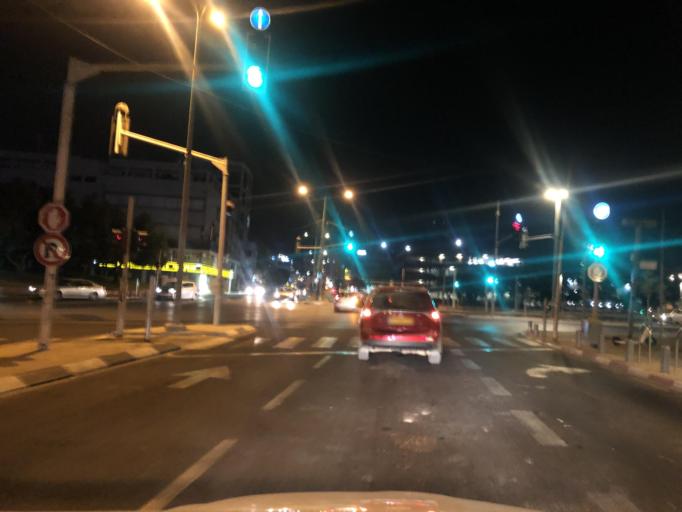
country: IL
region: Tel Aviv
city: Yafo
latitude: 32.0528
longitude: 34.7650
